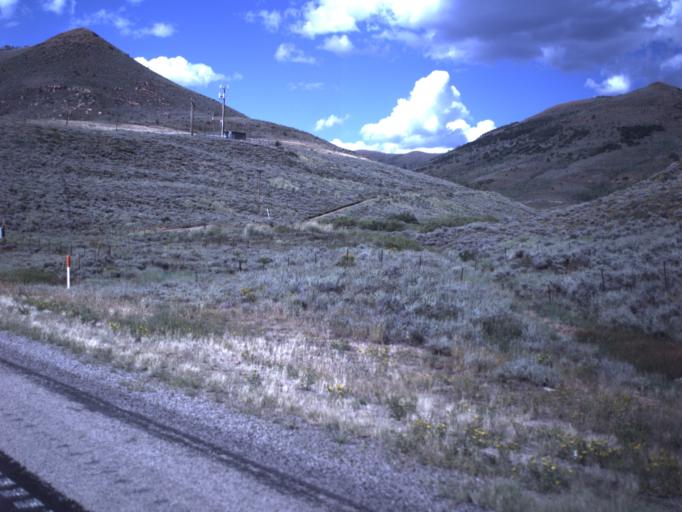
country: US
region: Utah
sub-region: Wasatch County
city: Heber
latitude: 40.2186
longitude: -111.1040
